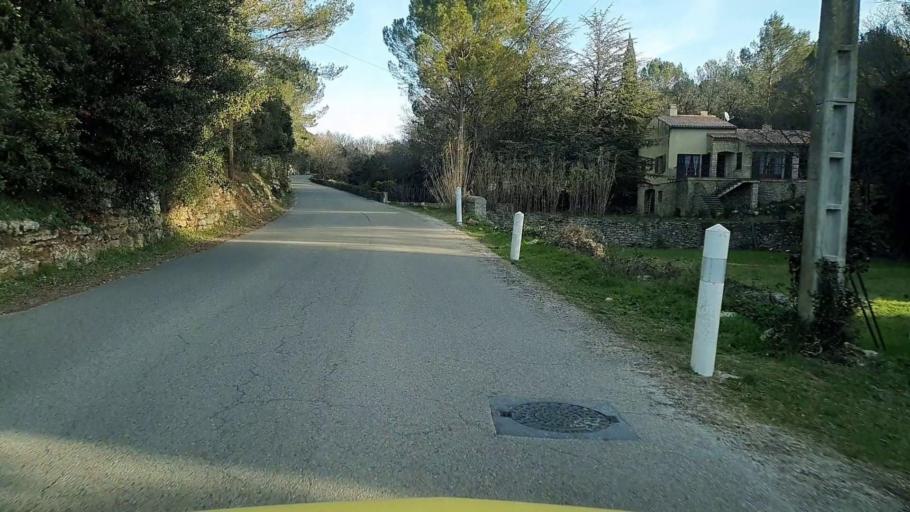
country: FR
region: Languedoc-Roussillon
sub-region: Departement du Gard
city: Castillon-du-Gard
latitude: 43.9641
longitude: 4.5542
